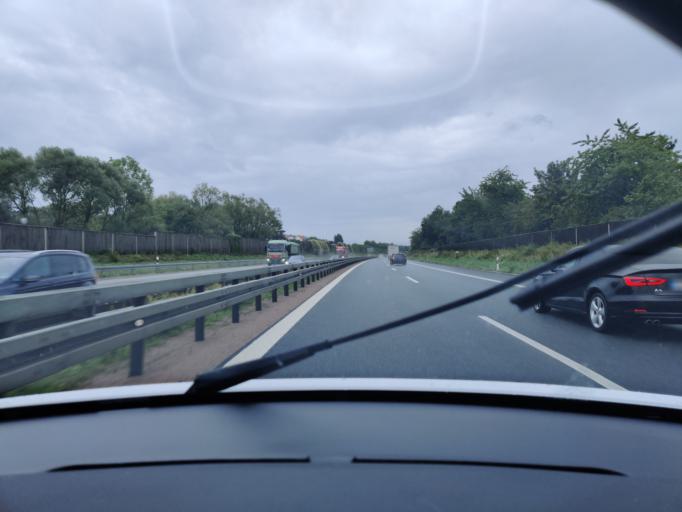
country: DE
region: Bavaria
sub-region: Upper Palatinate
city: Pfreimd
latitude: 49.5016
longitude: 12.1846
